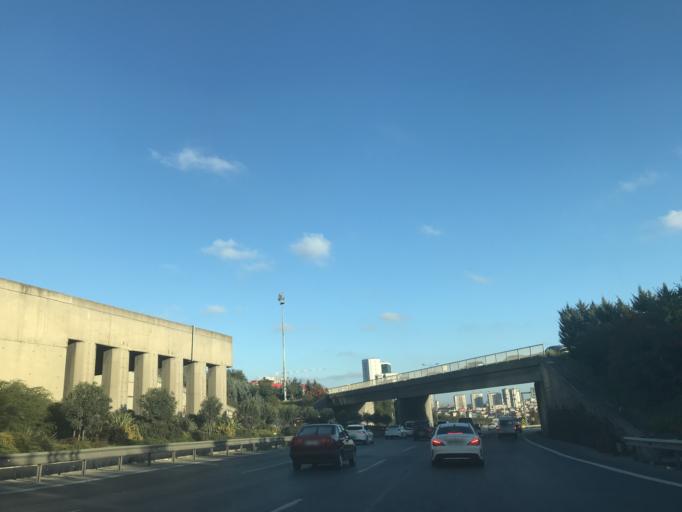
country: TR
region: Istanbul
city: Mahmutbey
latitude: 41.0614
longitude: 28.8413
